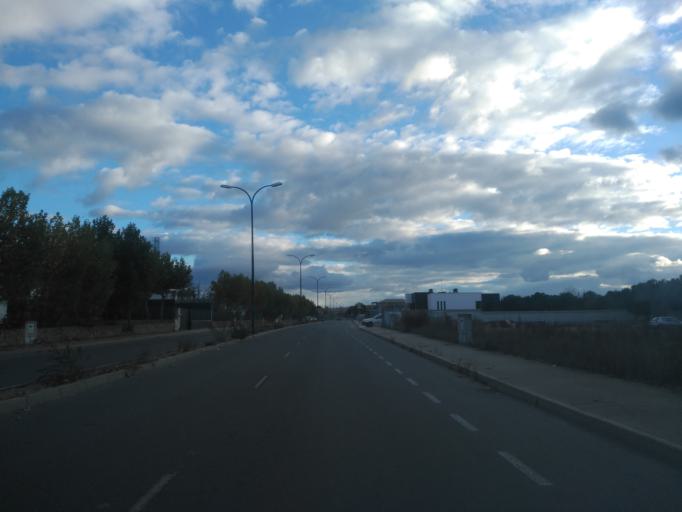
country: ES
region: Castille and Leon
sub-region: Provincia de Salamanca
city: Villamayor
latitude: 40.9879
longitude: -5.7140
